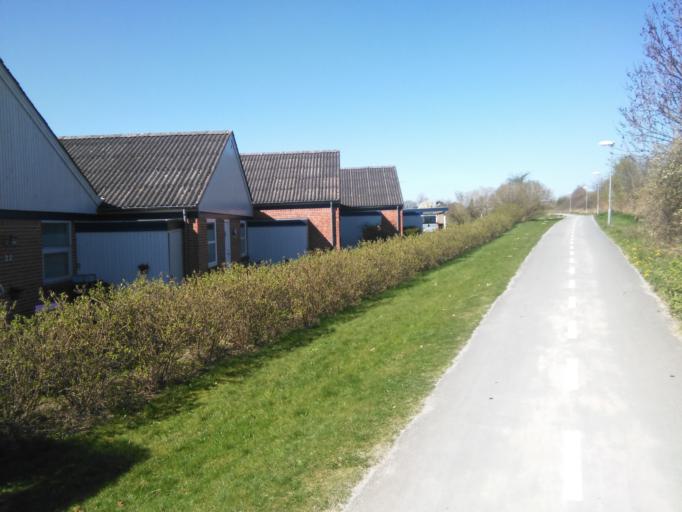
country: DK
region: Central Jutland
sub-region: Arhus Kommune
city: Marslet
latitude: 56.0694
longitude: 10.1621
